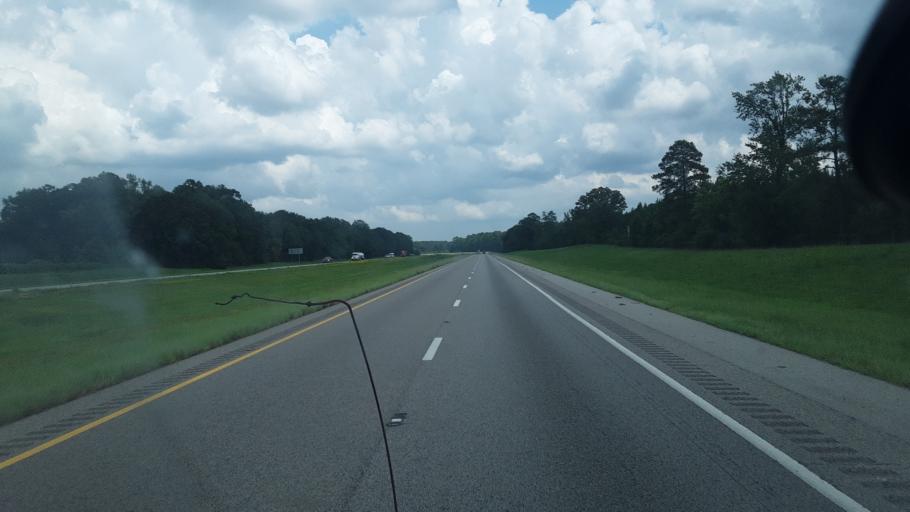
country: US
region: South Carolina
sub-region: Kershaw County
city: Camden
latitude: 34.2143
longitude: -80.5711
